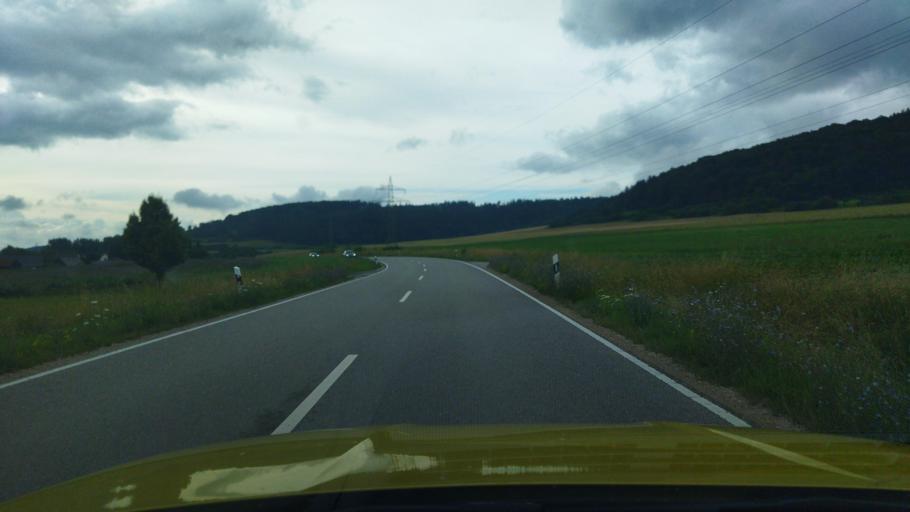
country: DE
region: Bavaria
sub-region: Regierungsbezirk Mittelfranken
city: Greding
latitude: 49.0610
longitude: 11.3297
